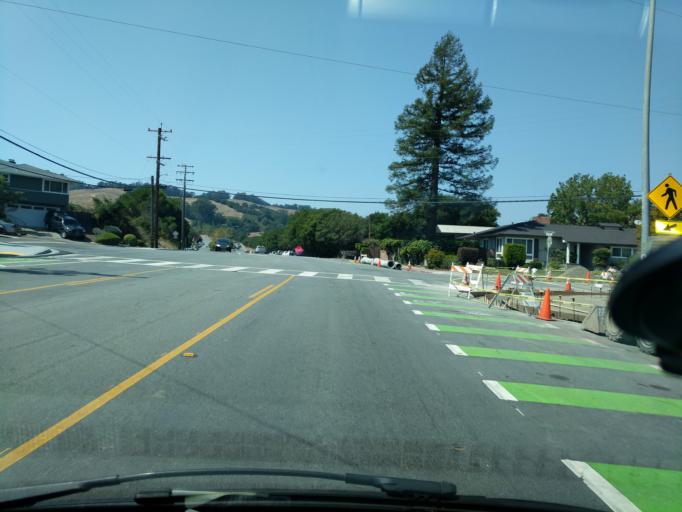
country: US
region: California
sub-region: Alameda County
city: Castro Valley
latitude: 37.7131
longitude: -122.0983
